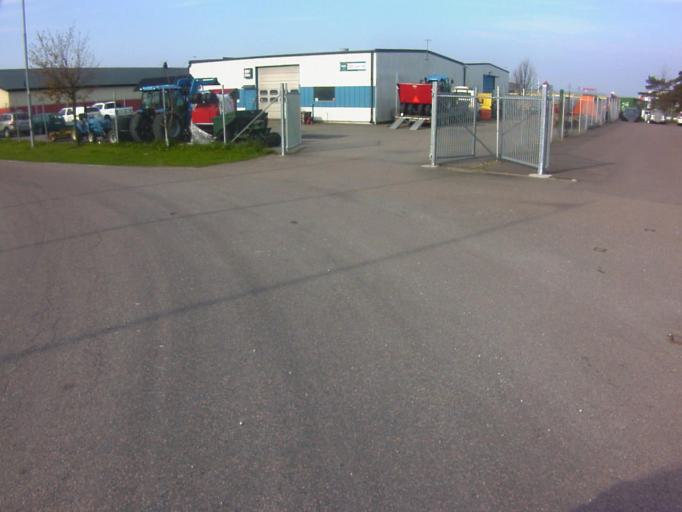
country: SE
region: Skane
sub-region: Kavlinge Kommun
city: Loddekopinge
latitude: 55.7704
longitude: 12.9965
